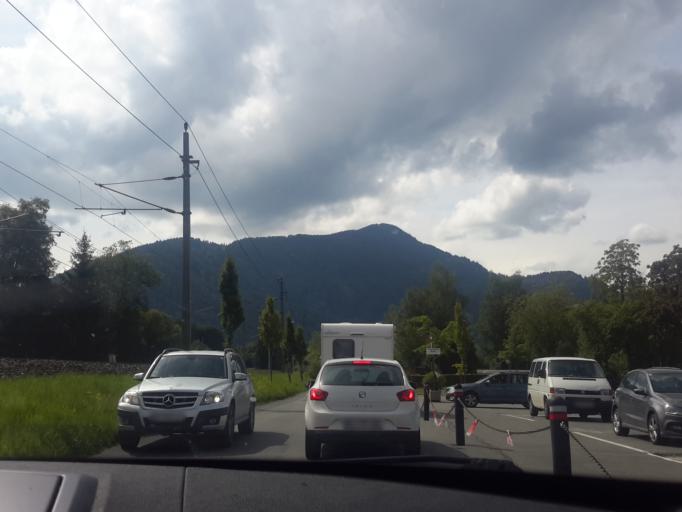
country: AT
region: Tyrol
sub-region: Politischer Bezirk Kitzbuhel
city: Reith bei Kitzbuhel
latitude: 47.4558
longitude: 12.3648
